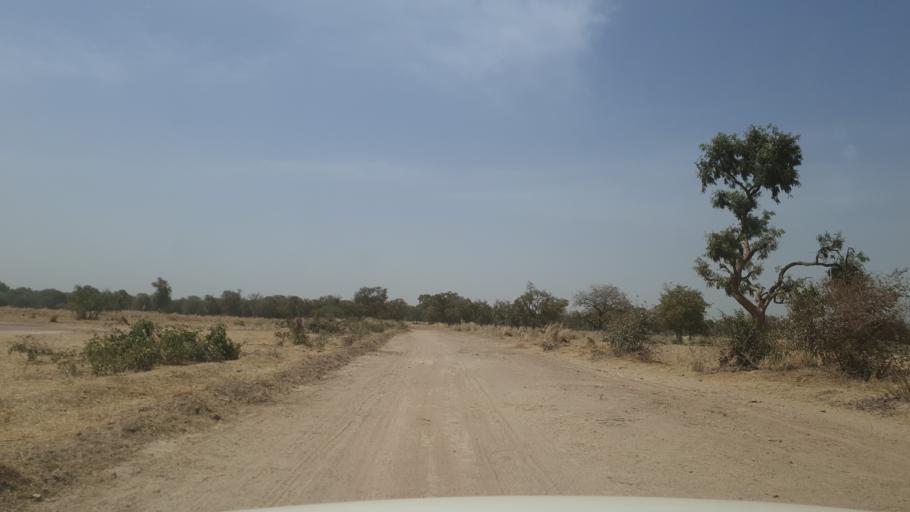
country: ML
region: Koulikoro
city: Kolokani
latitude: 13.4777
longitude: -8.1833
